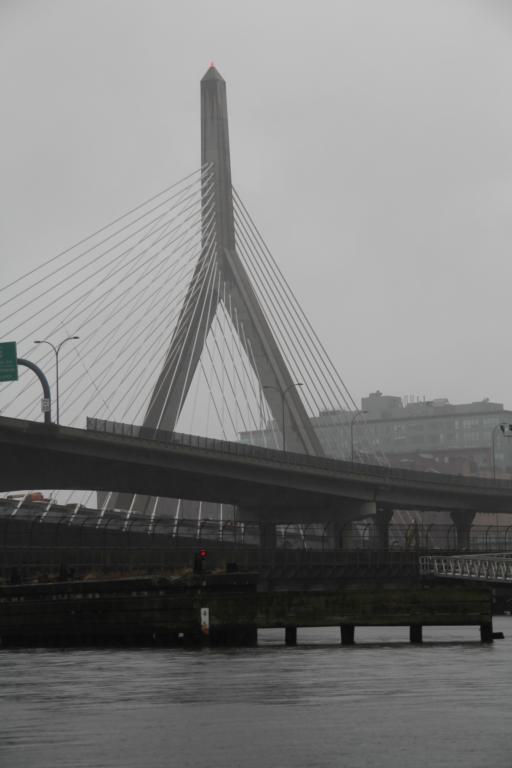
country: US
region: Massachusetts
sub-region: Suffolk County
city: Boston
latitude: 42.3687
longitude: -71.0632
